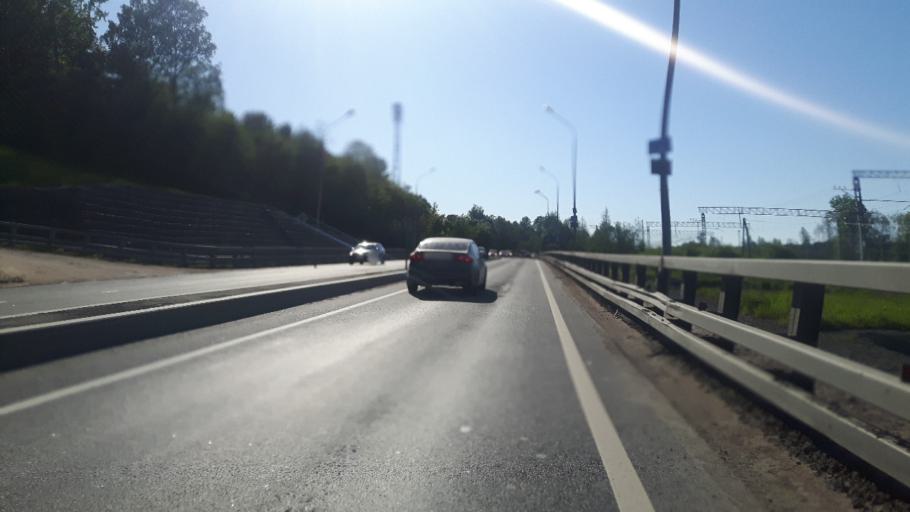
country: RU
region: St.-Petersburg
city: Bol'shaya Izhora
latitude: 59.9266
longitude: 29.6650
